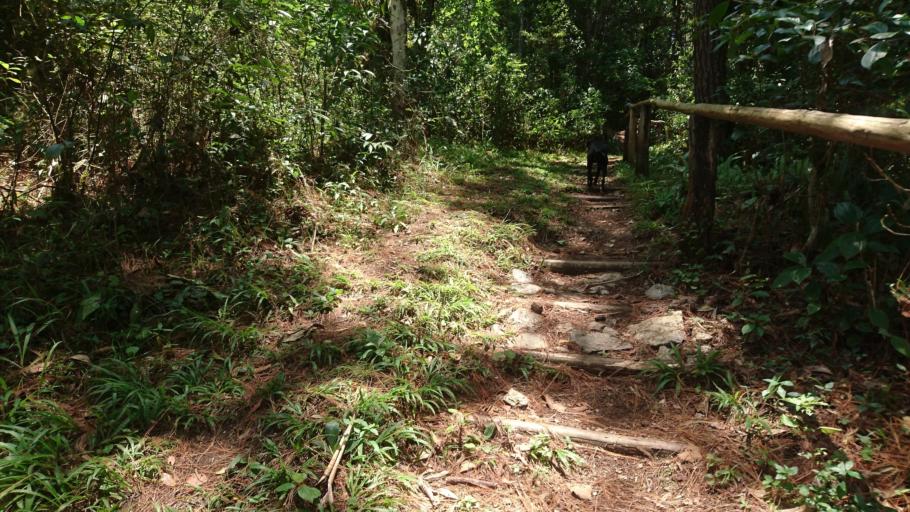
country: GT
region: Huehuetenango
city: Union
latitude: 16.1305
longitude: -91.7308
